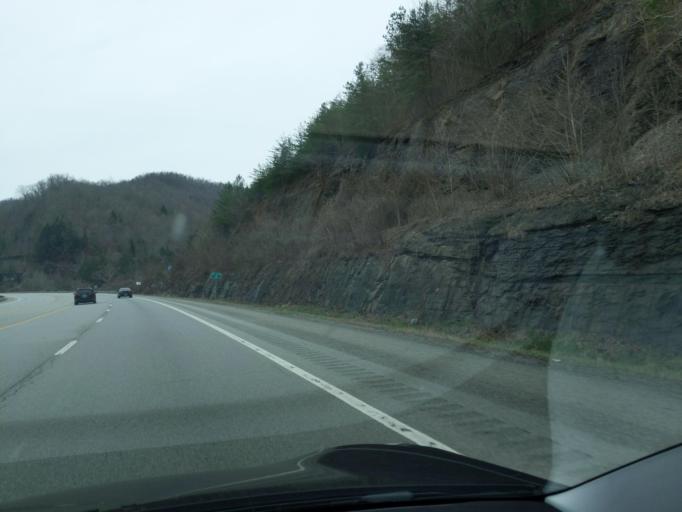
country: US
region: Kentucky
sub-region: Bell County
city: Pineville
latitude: 36.7760
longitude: -83.7363
